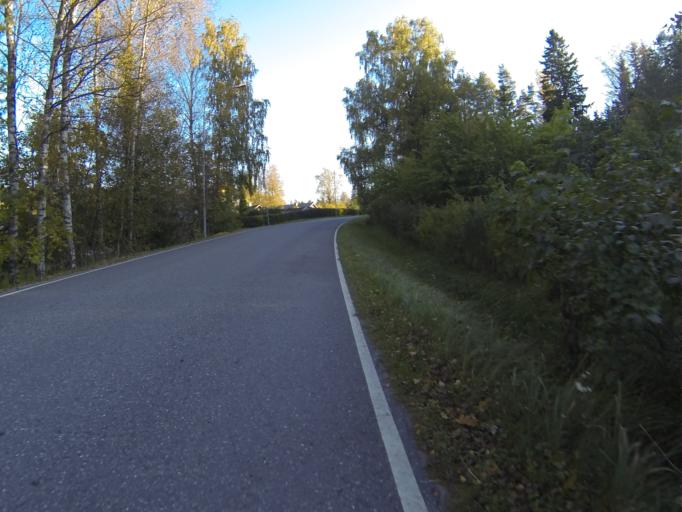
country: FI
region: Varsinais-Suomi
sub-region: Salo
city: Saerkisalo
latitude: 60.2129
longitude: 22.9198
